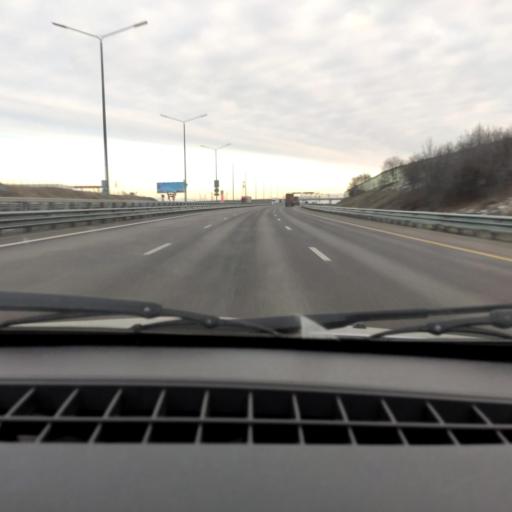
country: RU
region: Voronezj
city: Ramon'
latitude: 51.8241
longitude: 39.2459
